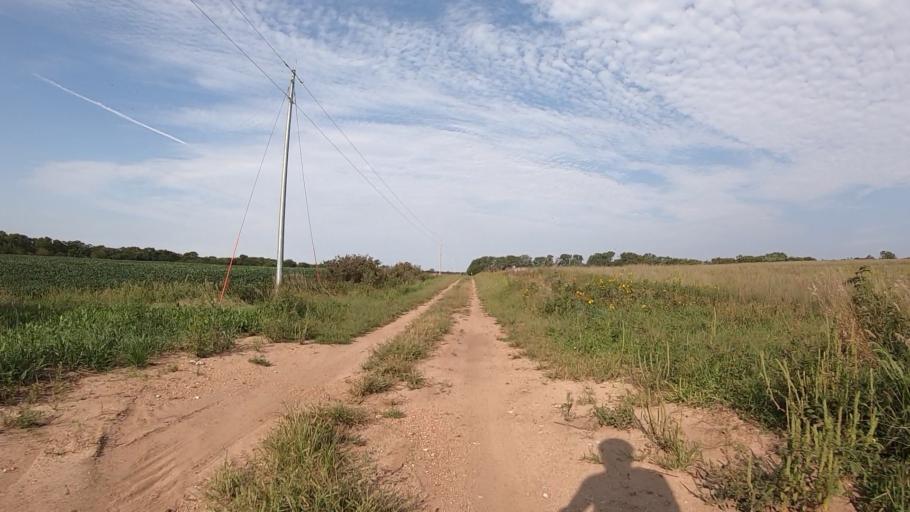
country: US
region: Kansas
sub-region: Washington County
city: Washington
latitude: 39.6714
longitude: -96.9397
